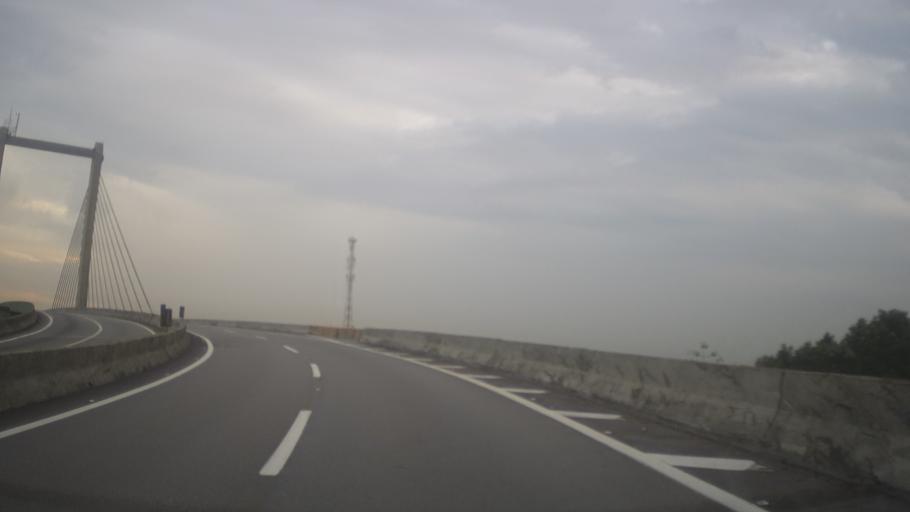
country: BR
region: Sao Paulo
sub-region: Cubatao
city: Cubatao
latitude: -23.9259
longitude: -46.4344
